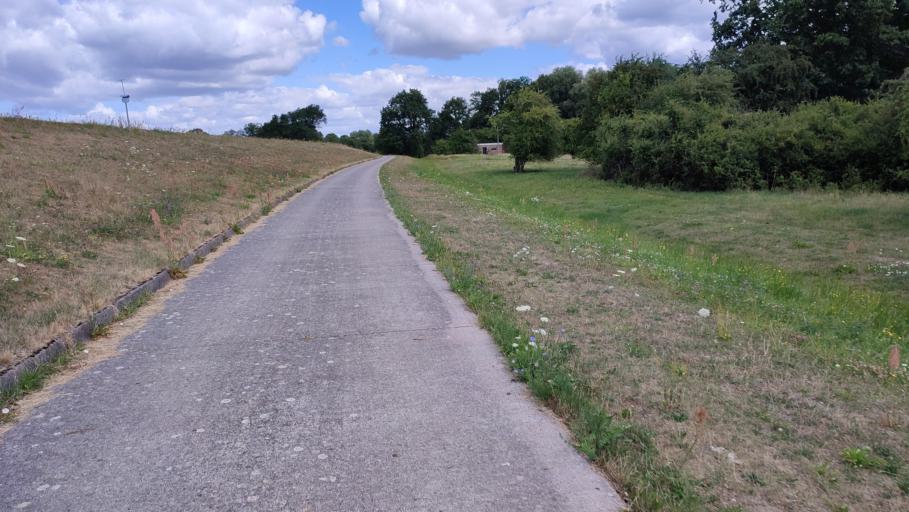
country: DE
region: Lower Saxony
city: Hitzacker
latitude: 53.1985
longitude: 10.9806
